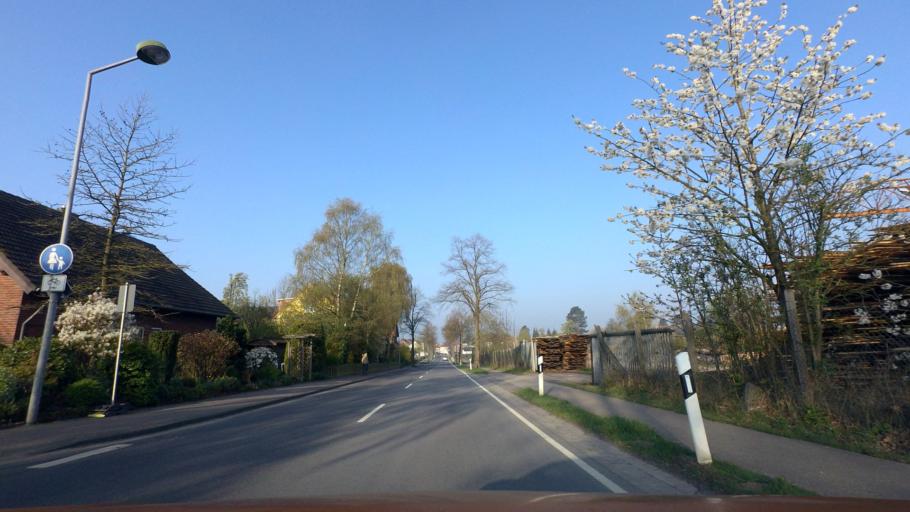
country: DE
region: Lower Saxony
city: Neuenkirchen
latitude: 52.1819
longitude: 8.4287
